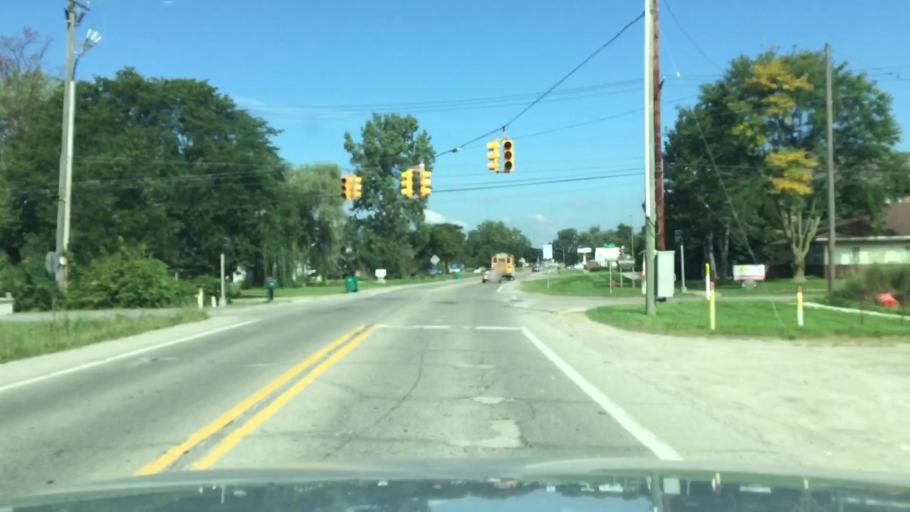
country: US
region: Michigan
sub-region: Wayne County
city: Belleville
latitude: 42.1970
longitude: -83.4849
